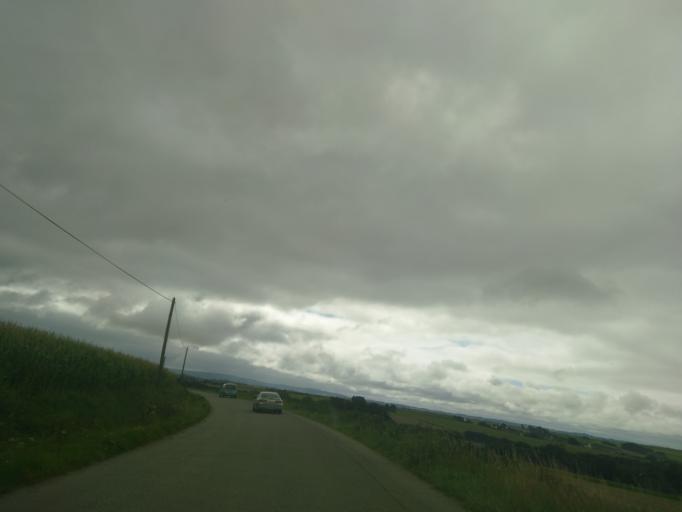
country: FR
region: Brittany
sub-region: Departement du Finistere
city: Plomodiern
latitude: 48.1640
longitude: -4.2608
